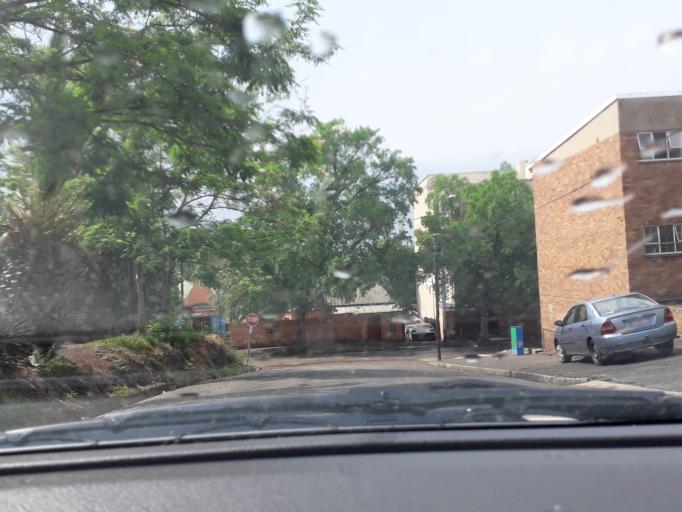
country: ZA
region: Gauteng
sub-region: City of Johannesburg Metropolitan Municipality
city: Johannesburg
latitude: -26.1838
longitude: 28.0689
